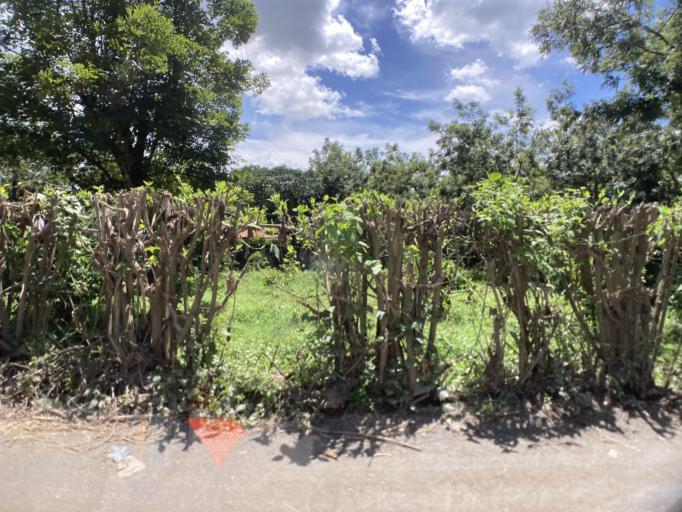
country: GT
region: Sacatepequez
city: Antigua Guatemala
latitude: 14.5403
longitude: -90.7354
